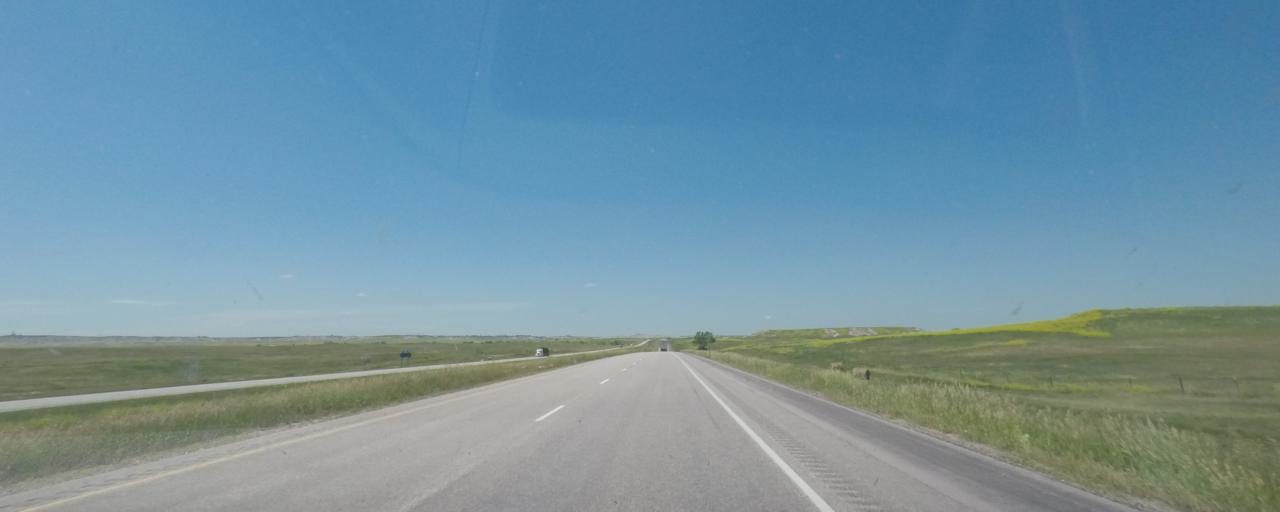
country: US
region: South Dakota
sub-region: Haakon County
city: Philip
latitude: 43.9513
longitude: -102.1664
